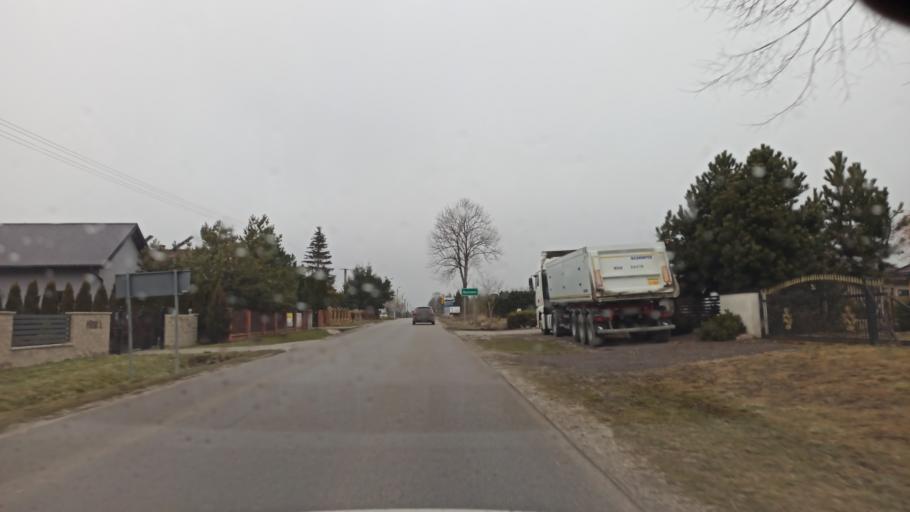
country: PL
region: Lublin Voivodeship
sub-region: Powiat lubelski
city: Bychawa
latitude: 51.0036
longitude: 22.5585
